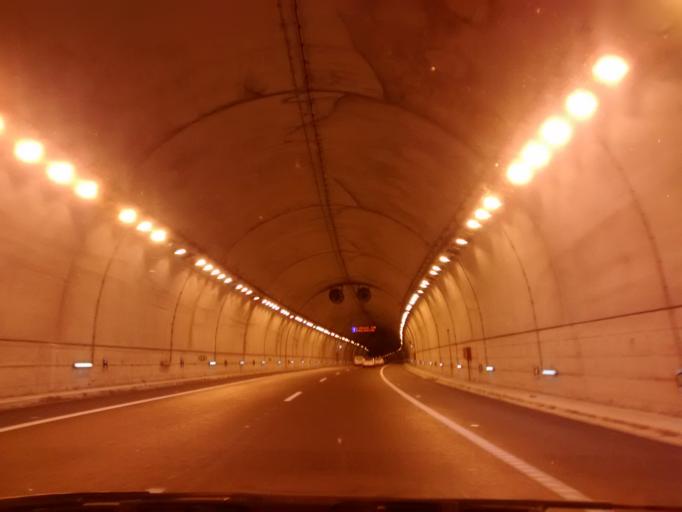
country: ES
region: Cantabria
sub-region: Provincia de Cantabria
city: Camargo
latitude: 43.3919
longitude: -3.8664
